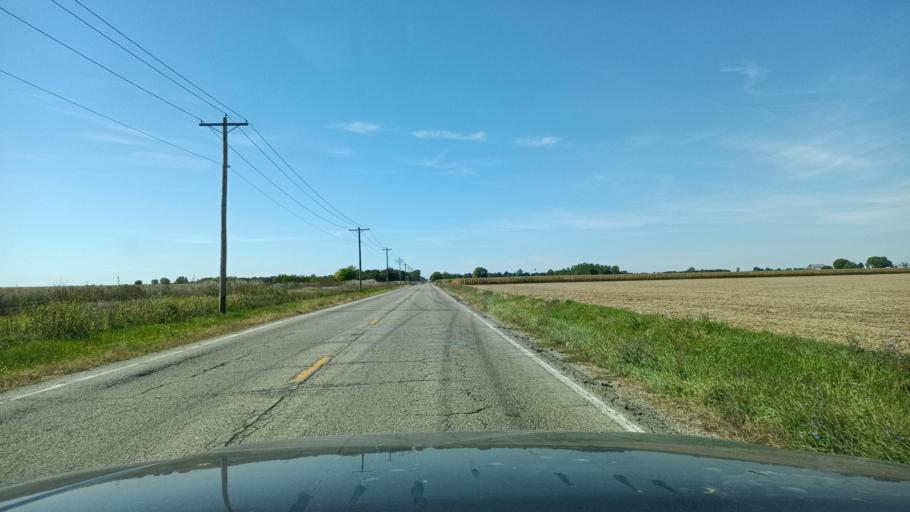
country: US
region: Illinois
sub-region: Champaign County
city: Mahomet
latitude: 40.2073
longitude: -88.4796
